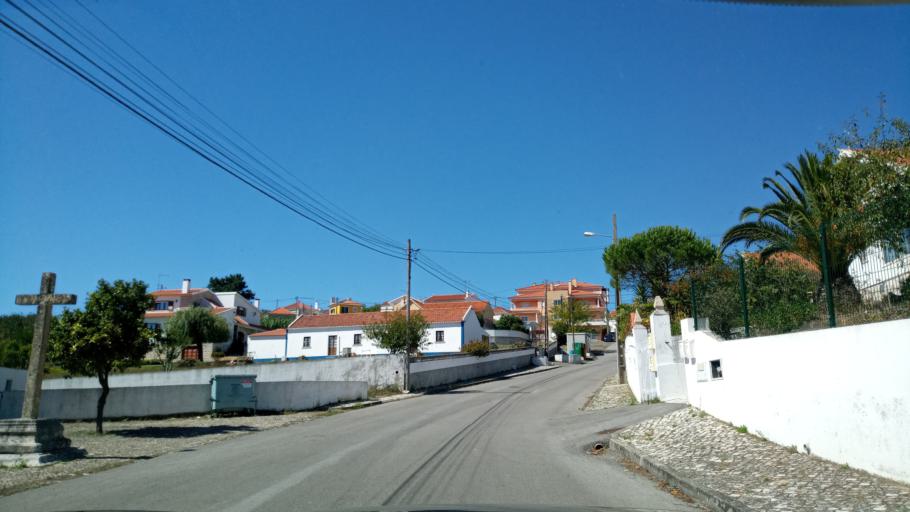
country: PT
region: Lisbon
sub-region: Mafra
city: Malveira
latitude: 38.9208
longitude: -9.2904
